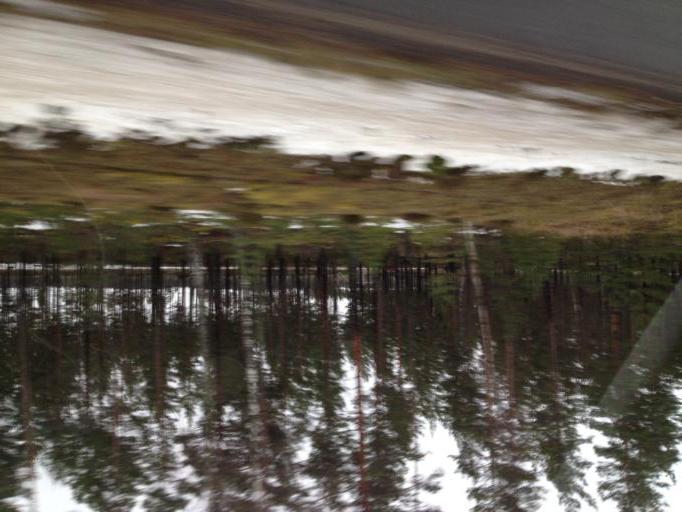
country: FI
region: Uusimaa
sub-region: Raaseporin
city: Hanko
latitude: 59.8534
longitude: 23.0118
